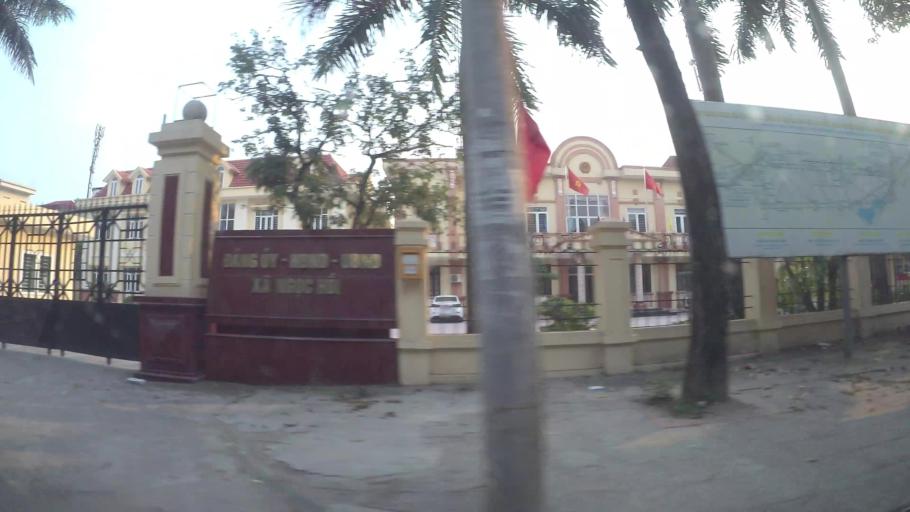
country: VN
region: Ha Noi
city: Van Dien
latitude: 20.9235
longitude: 105.8427
